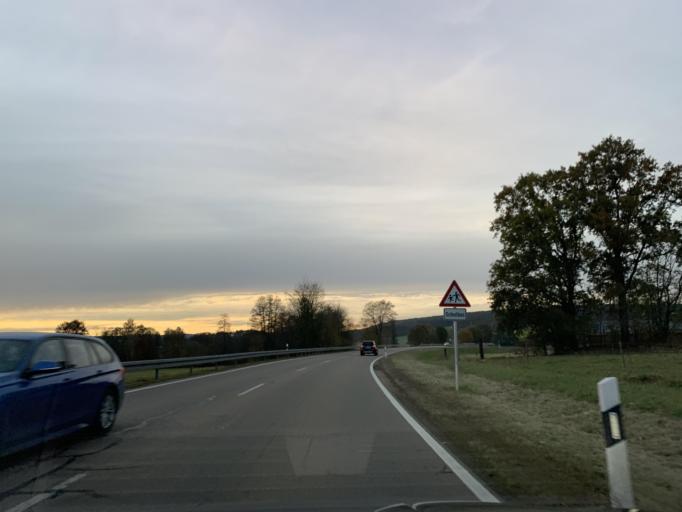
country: DE
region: Bavaria
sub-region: Upper Palatinate
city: Neunburg vorm Wald
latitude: 49.3533
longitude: 12.3780
